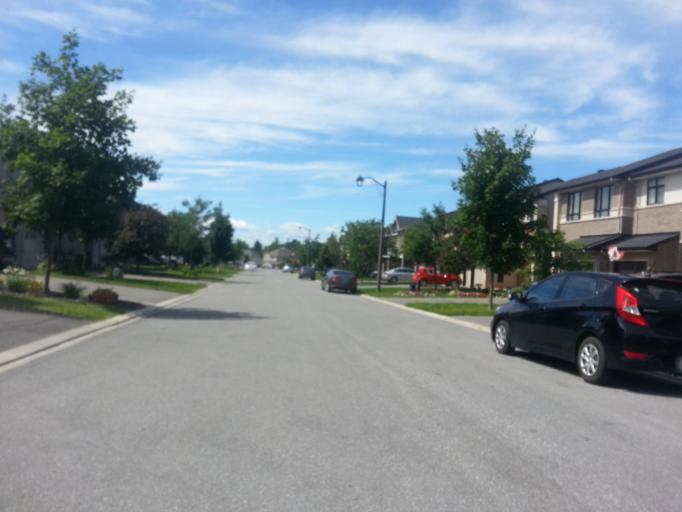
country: CA
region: Ontario
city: Bells Corners
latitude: 45.3233
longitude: -75.9311
